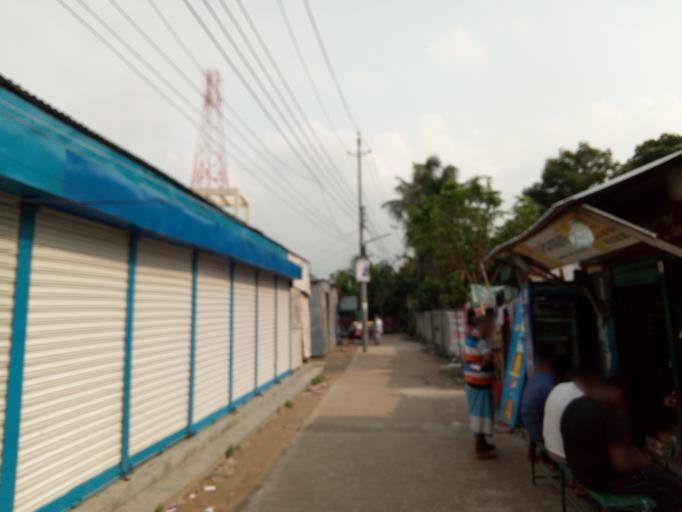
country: BD
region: Dhaka
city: Paltan
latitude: 23.7599
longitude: 90.4641
